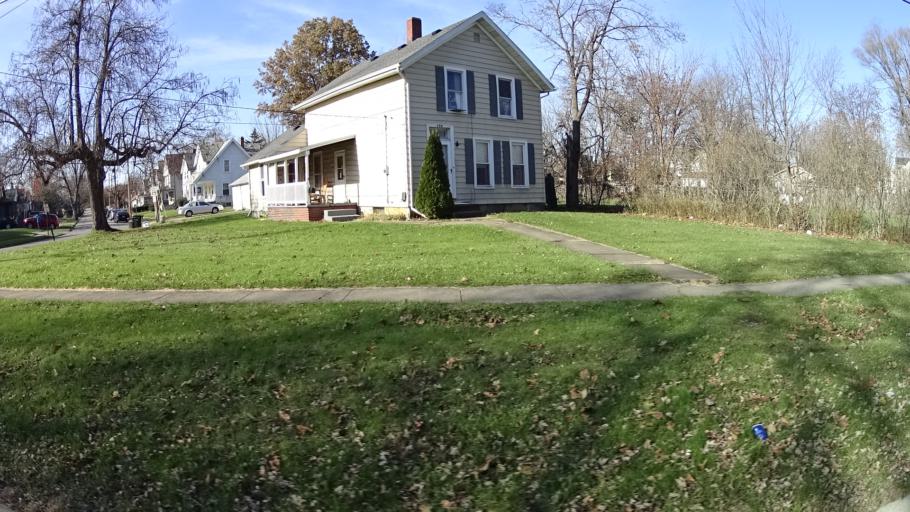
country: US
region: Ohio
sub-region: Lorain County
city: Elyria
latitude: 41.3761
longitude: -82.1131
